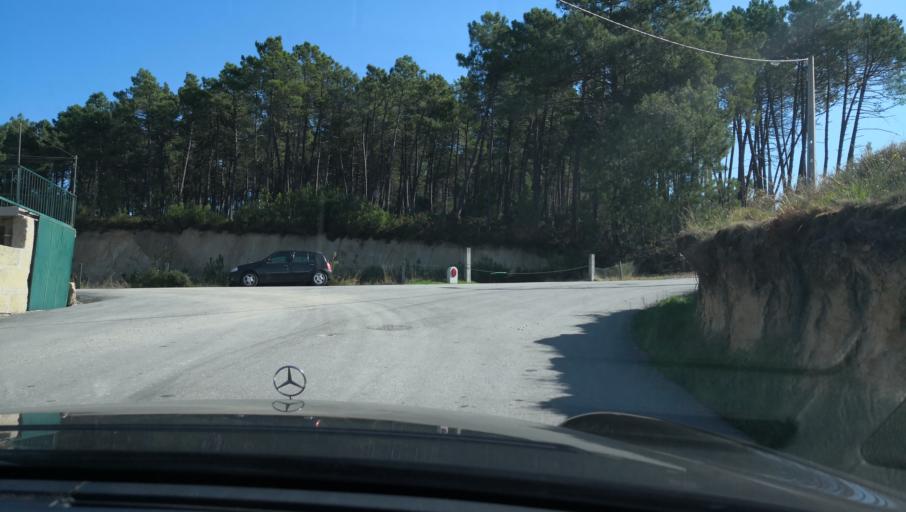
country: PT
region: Vila Real
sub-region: Vila Real
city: Vila Real
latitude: 41.3208
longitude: -7.6760
